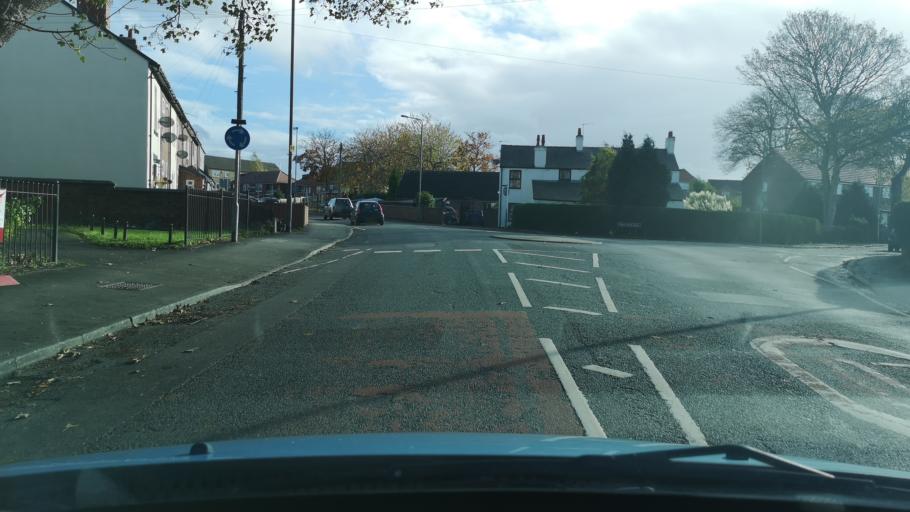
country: GB
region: England
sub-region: City and Borough of Wakefield
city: Crofton
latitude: 53.6548
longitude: -1.4274
